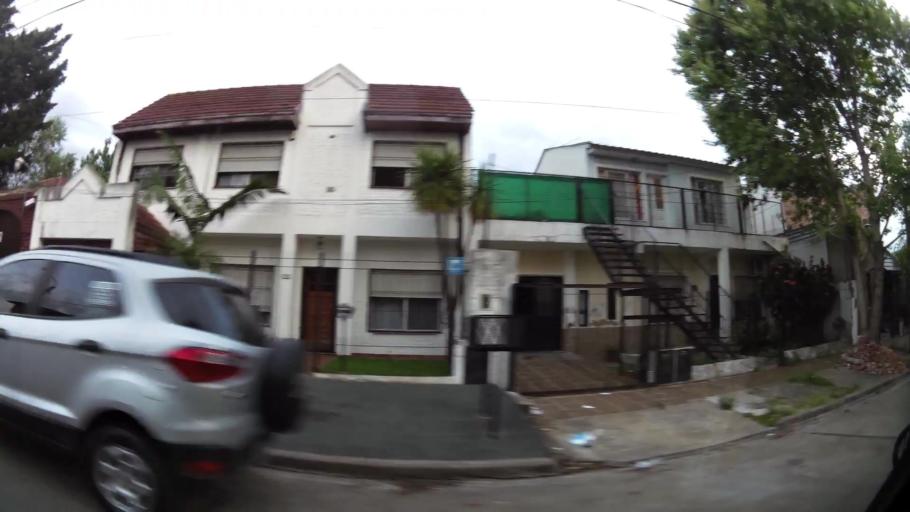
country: AR
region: Buenos Aires
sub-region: Partido de Quilmes
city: Quilmes
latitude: -34.7407
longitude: -58.2423
